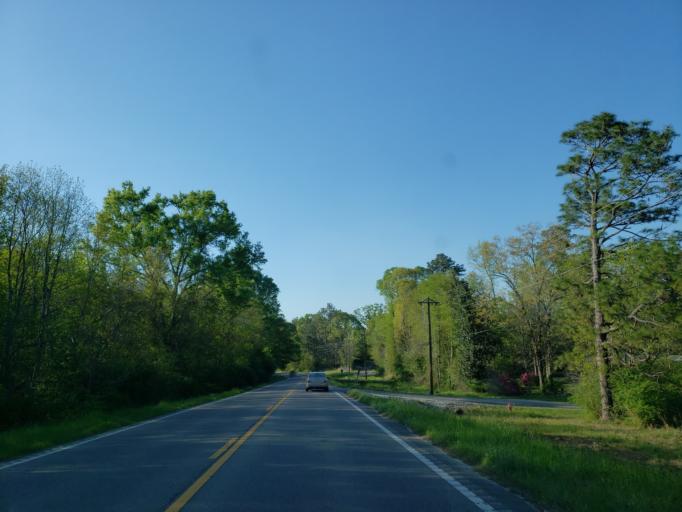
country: US
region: Mississippi
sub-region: Jones County
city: Laurel
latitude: 31.6452
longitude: -89.0985
